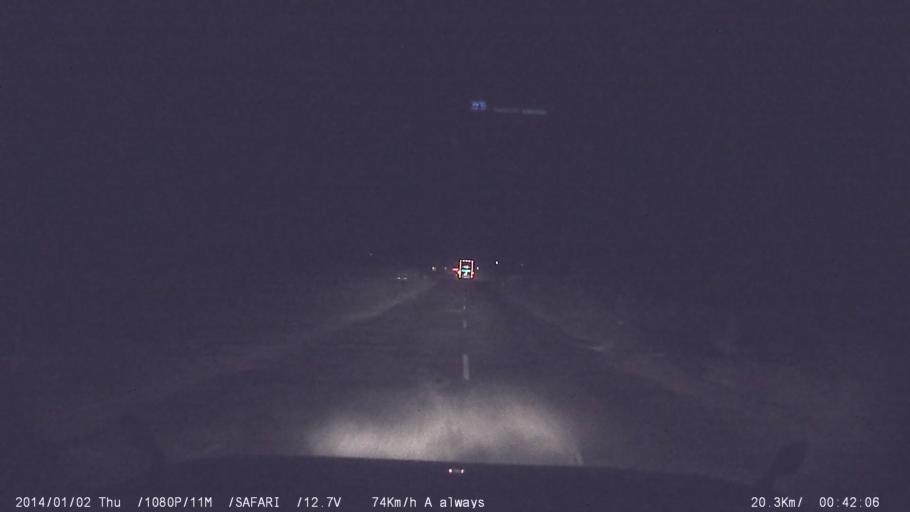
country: IN
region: Tamil Nadu
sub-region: Coimbatore
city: Madukkarai
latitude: 10.8548
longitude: 76.8514
